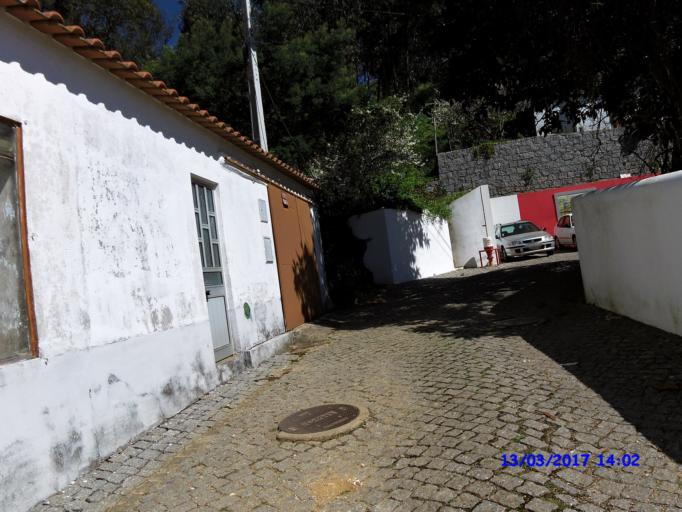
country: PT
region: Faro
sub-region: Monchique
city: Monchique
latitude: 37.3124
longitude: -8.6697
